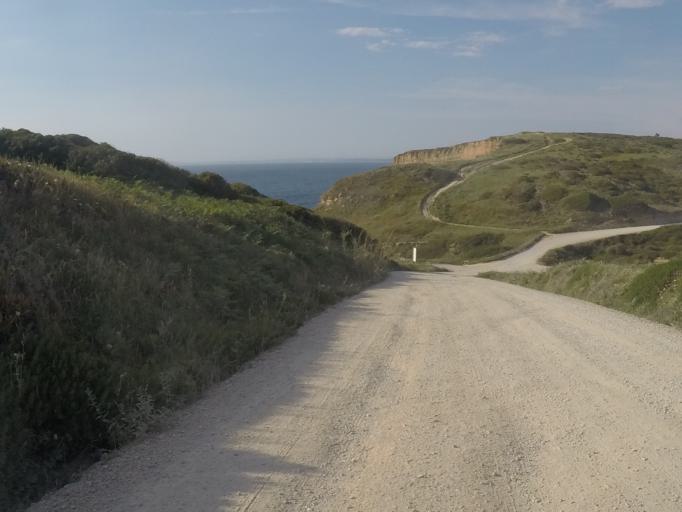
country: PT
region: Setubal
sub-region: Sesimbra
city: Sesimbra
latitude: 38.4513
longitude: -9.1987
